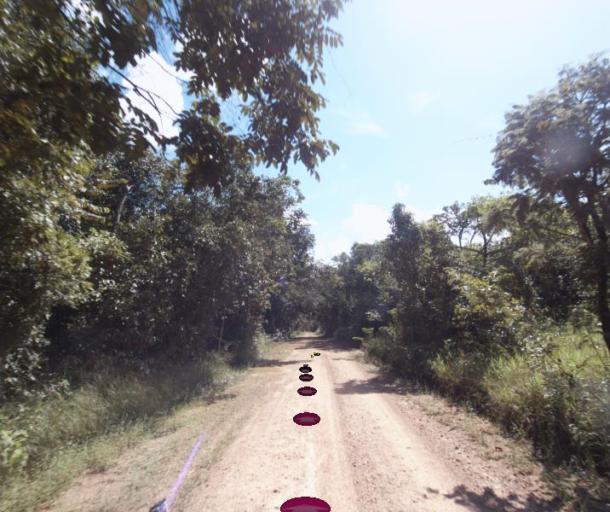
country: BR
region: Goias
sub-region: Pirenopolis
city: Pirenopolis
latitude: -15.7744
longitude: -49.0153
